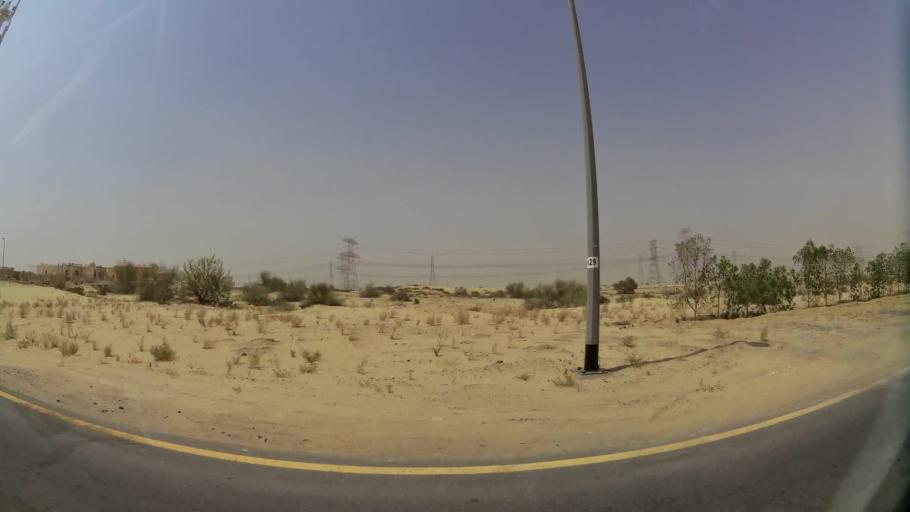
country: AE
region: Ash Shariqah
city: Sharjah
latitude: 25.2587
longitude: 55.4885
